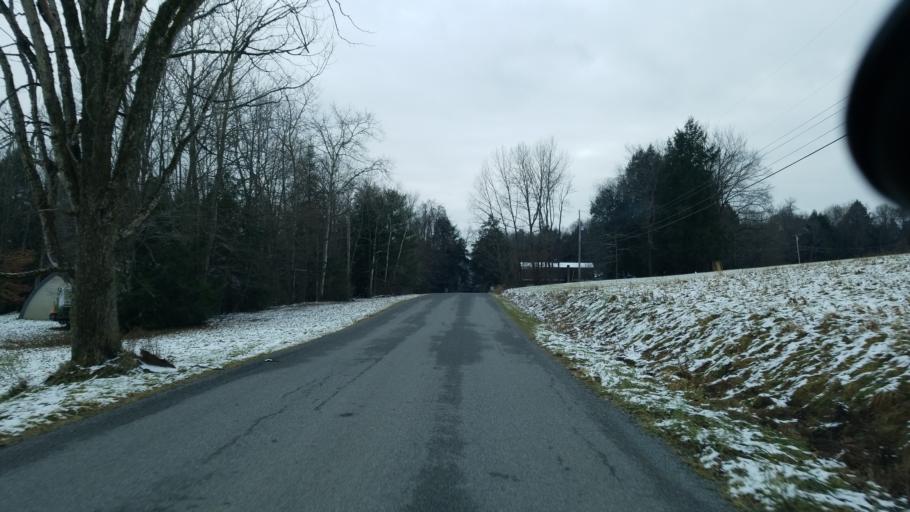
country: US
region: Pennsylvania
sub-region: Clearfield County
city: Treasure Lake
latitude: 41.0805
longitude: -78.6424
